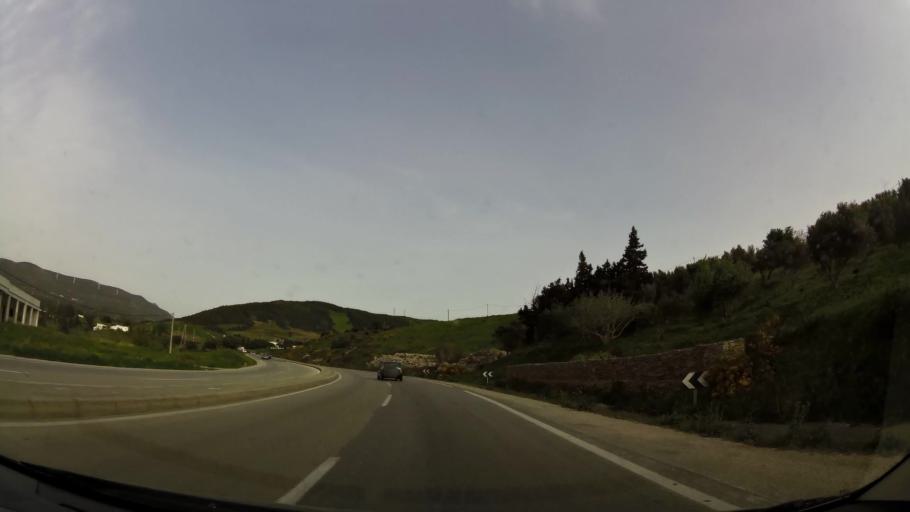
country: MA
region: Tanger-Tetouan
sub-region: Tanger-Assilah
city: Dar Chaoui
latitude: 35.5633
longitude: -5.6013
